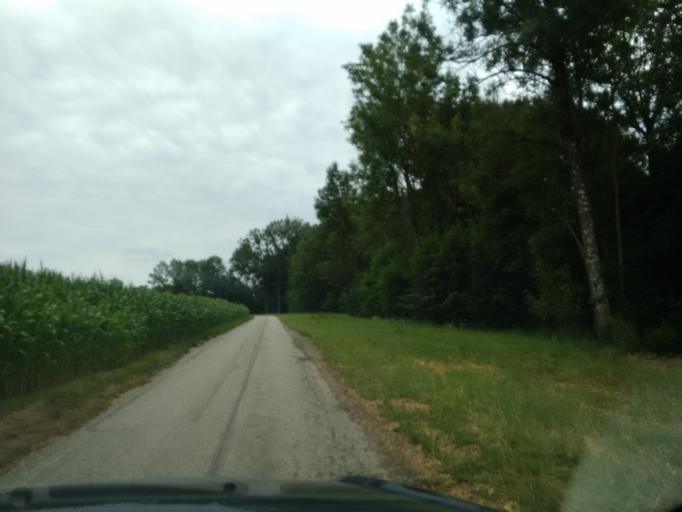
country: AT
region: Upper Austria
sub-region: Politischer Bezirk Grieskirchen
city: Bad Schallerbach
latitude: 48.2062
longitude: 13.9358
